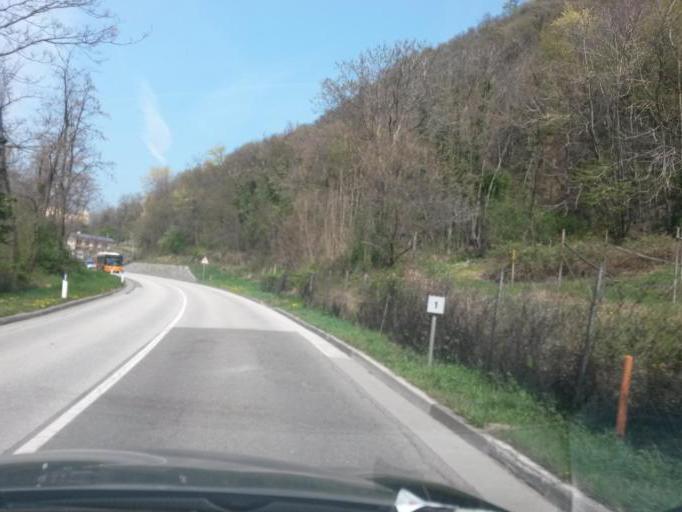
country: IT
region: Trentino-Alto Adige
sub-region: Bolzano
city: Sinigo
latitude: 46.6550
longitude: 11.1856
